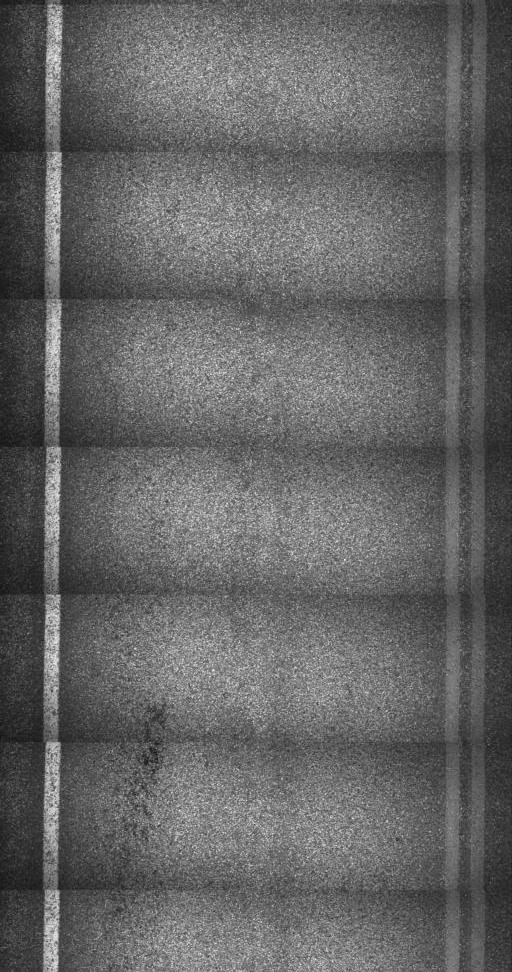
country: US
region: Vermont
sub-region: Grand Isle County
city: North Hero
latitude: 44.8536
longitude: -73.2597
